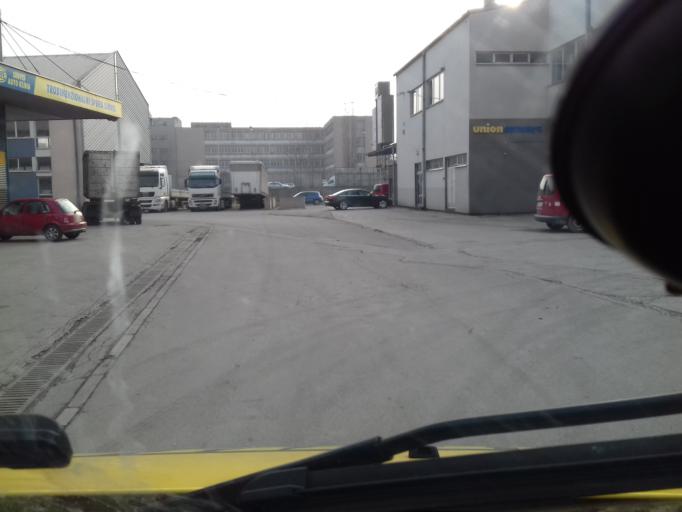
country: BA
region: Federation of Bosnia and Herzegovina
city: Zenica
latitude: 44.2131
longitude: 17.9085
